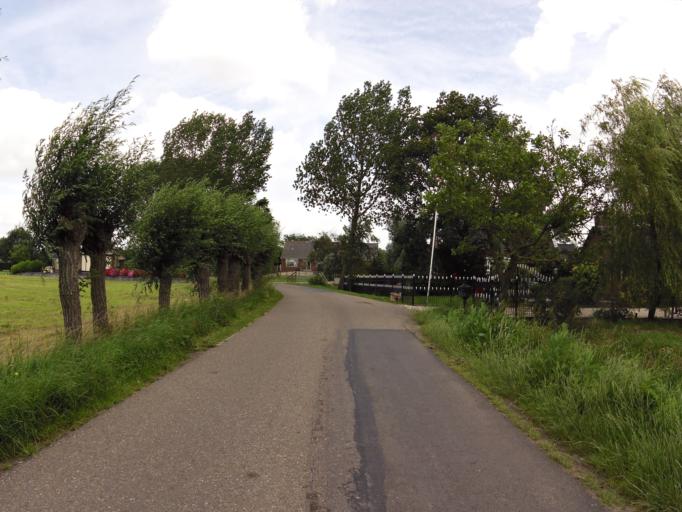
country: NL
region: South Holland
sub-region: Gemeente Gorinchem
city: Gorinchem
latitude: 51.8913
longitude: 4.9715
